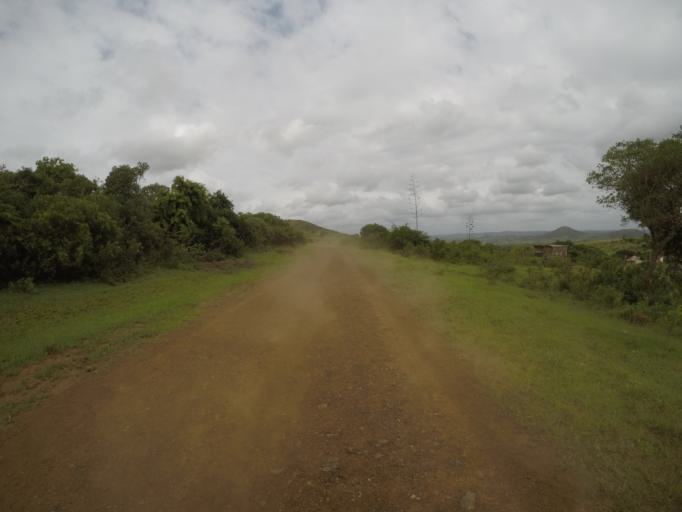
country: ZA
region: KwaZulu-Natal
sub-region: uThungulu District Municipality
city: Empangeni
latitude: -28.6138
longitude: 31.8971
